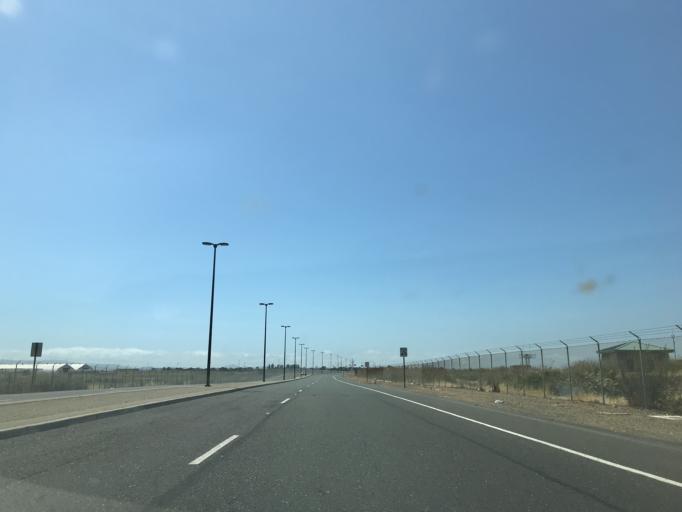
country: US
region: California
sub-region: Alameda County
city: Alameda
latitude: 37.7217
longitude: -122.2115
